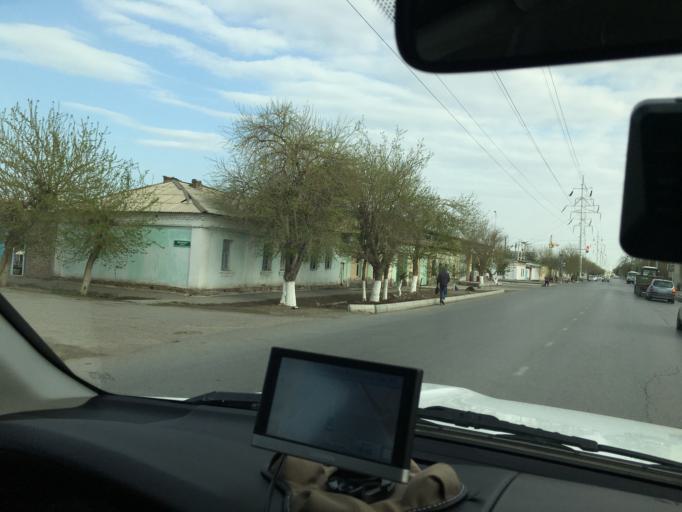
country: TM
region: Lebap
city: Turkmenabat
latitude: 39.0817
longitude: 63.5839
